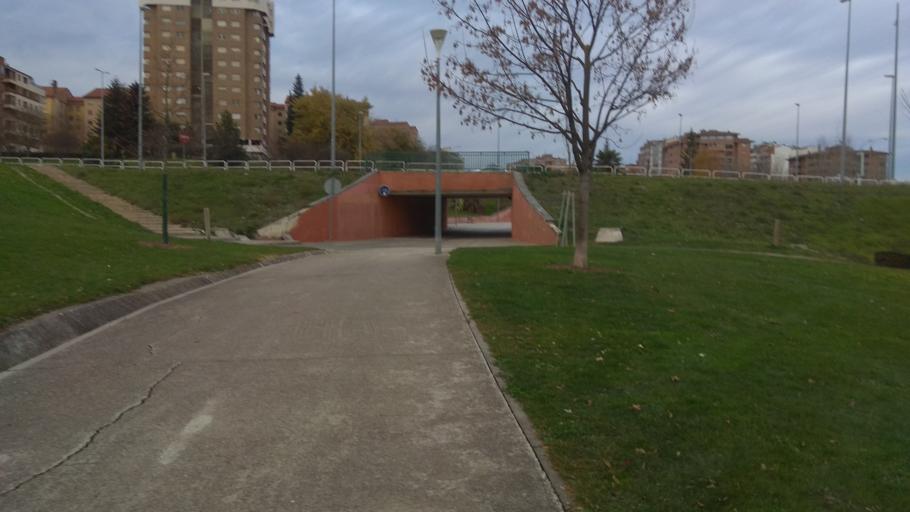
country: ES
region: Navarre
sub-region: Provincia de Navarra
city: Iturrama
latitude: 42.8011
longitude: -1.6503
